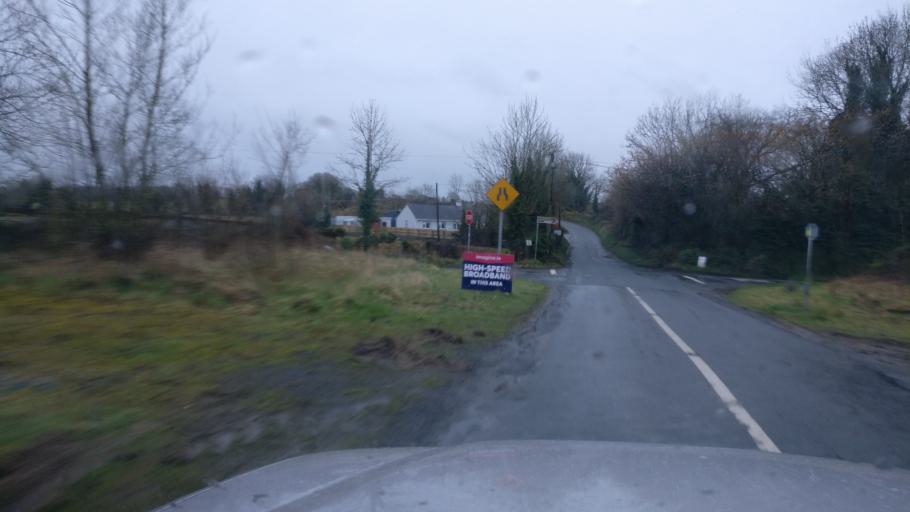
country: IE
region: Connaught
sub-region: County Galway
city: Ballinasloe
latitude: 53.3056
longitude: -8.2789
